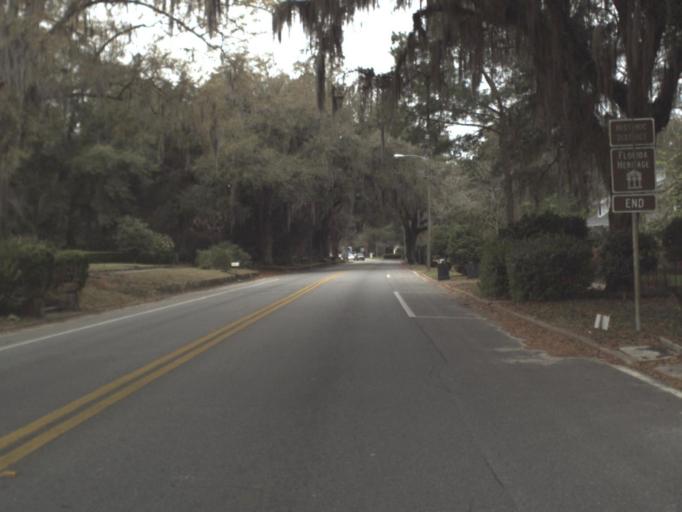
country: US
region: Florida
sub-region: Jefferson County
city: Monticello
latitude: 30.5452
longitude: -83.8751
